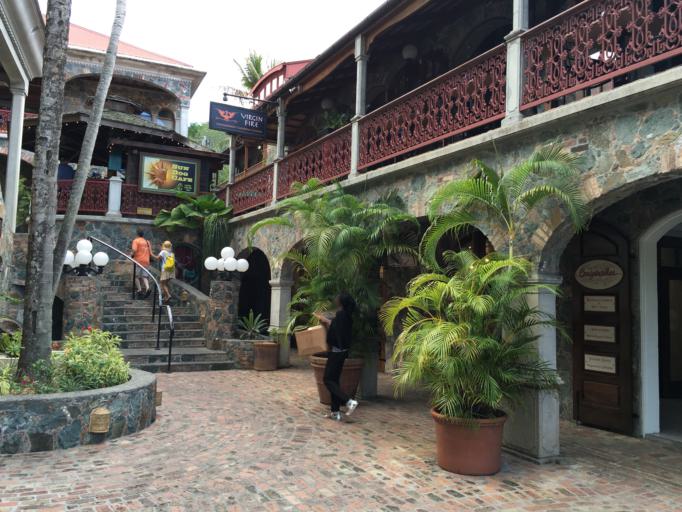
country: VI
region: Saint John Island
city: Cruz Bay
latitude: 18.3326
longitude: -64.7924
